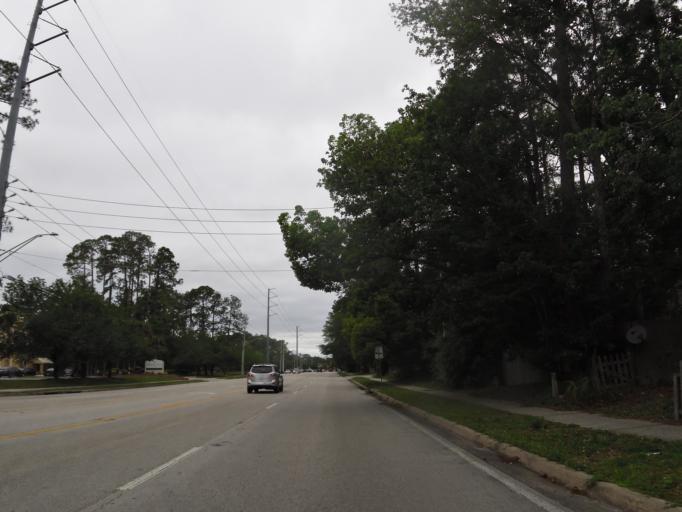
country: US
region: Florida
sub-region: Saint Johns County
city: Fruit Cove
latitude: 30.1798
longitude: -81.6059
